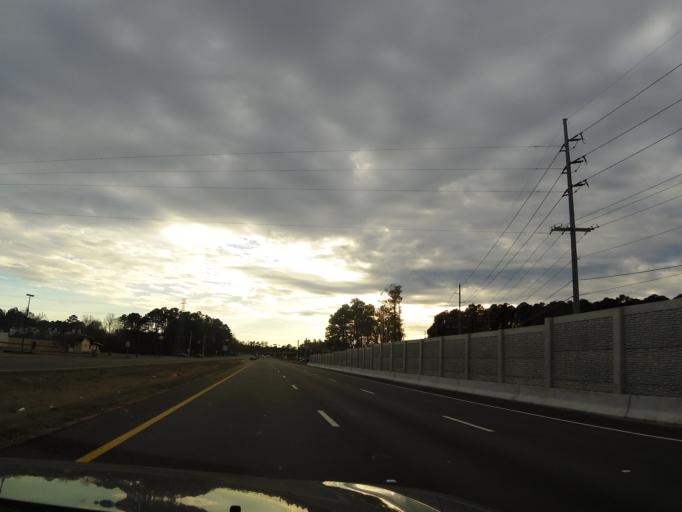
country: US
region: North Carolina
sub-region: Nash County
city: Rocky Mount
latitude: 35.9557
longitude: -77.8252
